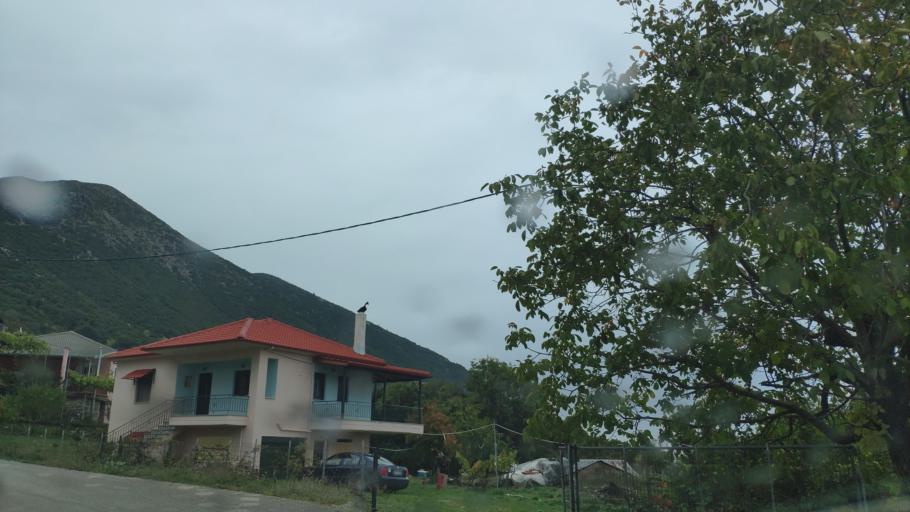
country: GR
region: Epirus
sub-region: Nomos Thesprotias
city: Paramythia
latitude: 39.4600
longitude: 20.6706
